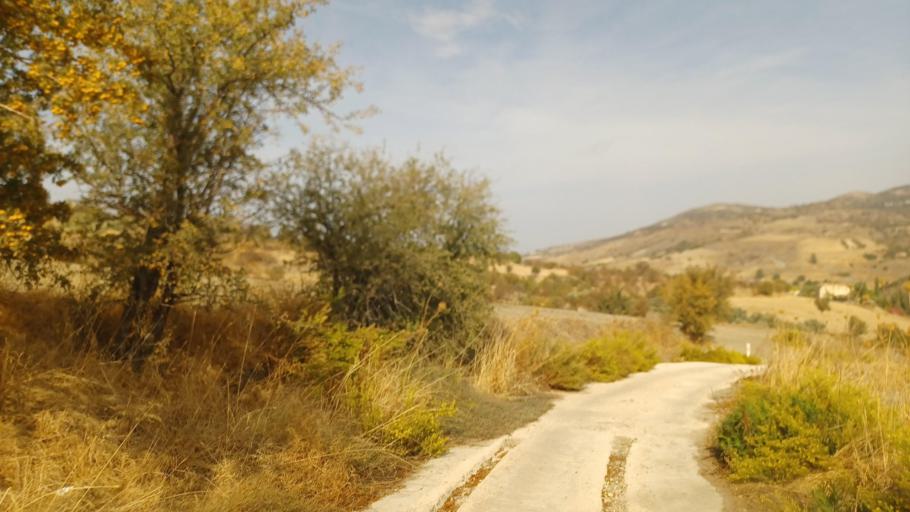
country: CY
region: Pafos
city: Polis
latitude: 34.9502
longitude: 32.5145
